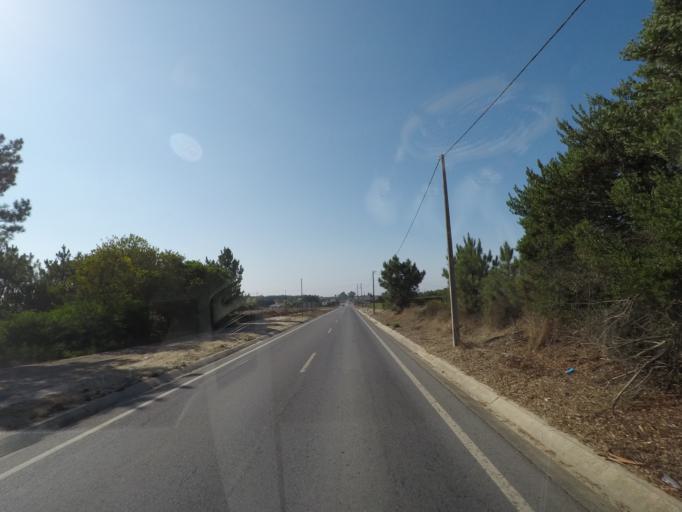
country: PT
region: Beja
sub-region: Odemira
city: Vila Nova de Milfontes
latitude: 37.6598
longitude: -8.7549
